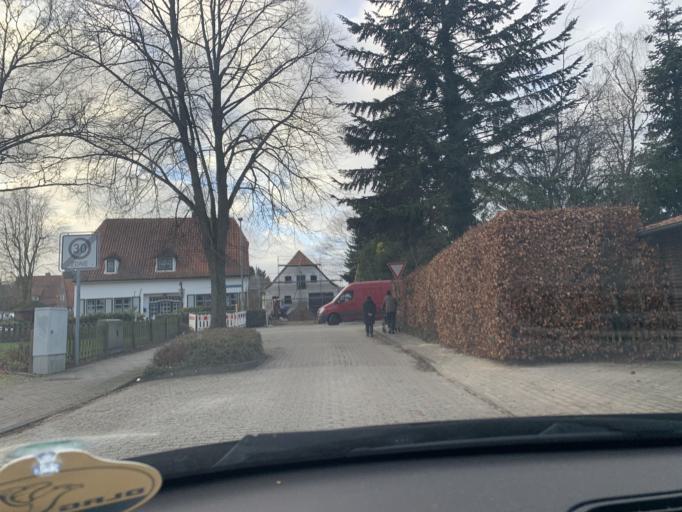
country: DE
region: Lower Saxony
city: Varel
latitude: 53.3952
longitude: 8.1481
